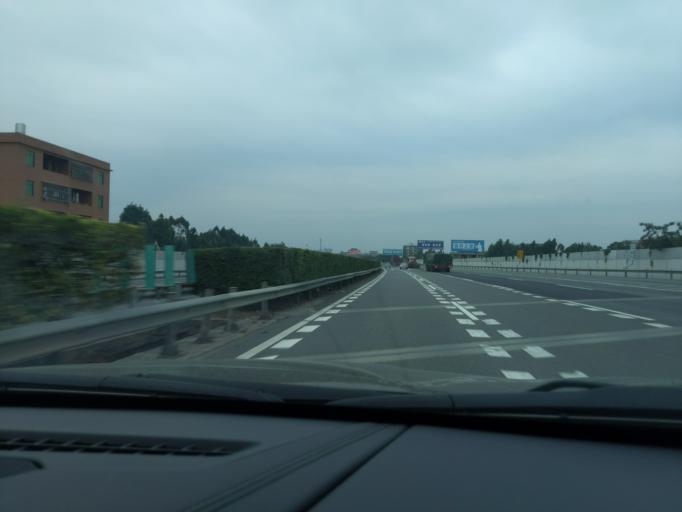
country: CN
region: Fujian
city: Anhai
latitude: 24.7314
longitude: 118.4175
